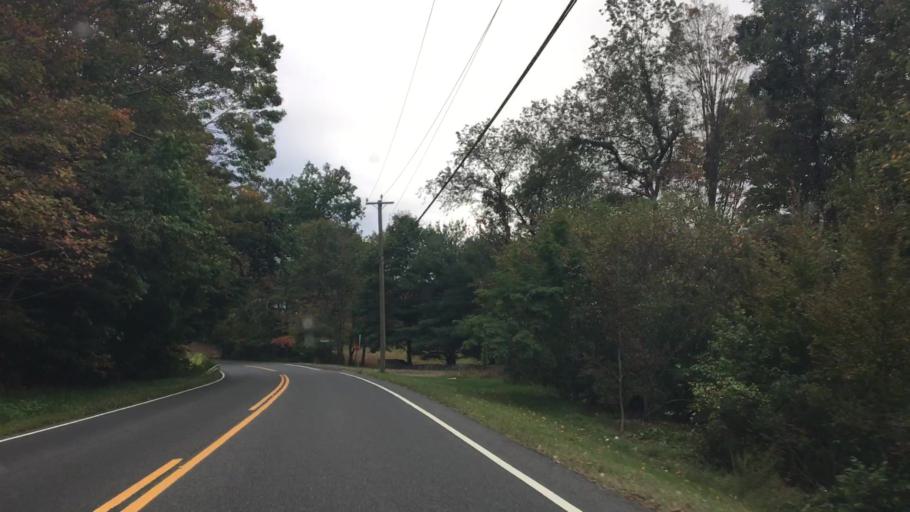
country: US
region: Connecticut
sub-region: New Haven County
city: Oxford
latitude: 41.4320
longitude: -73.1570
